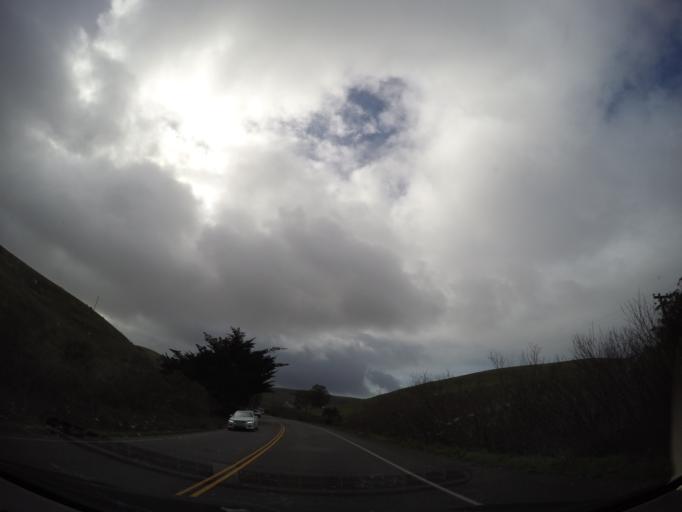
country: US
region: California
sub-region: Sonoma County
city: Bodega Bay
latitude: 38.3347
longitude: -122.9932
